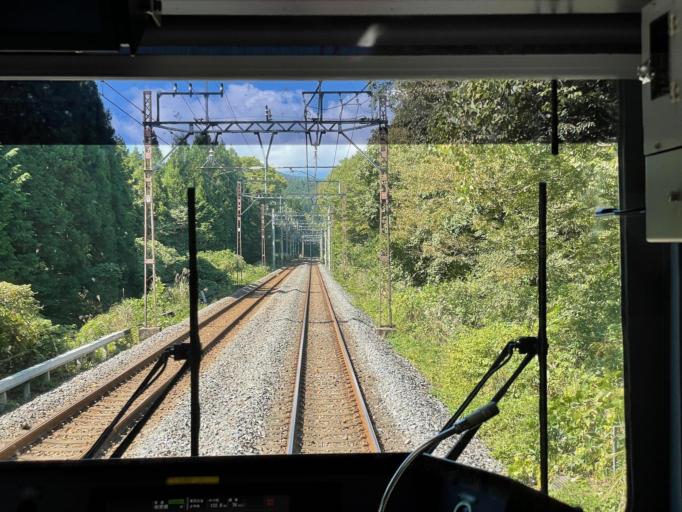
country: JP
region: Tochigi
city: Nikko
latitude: 36.7359
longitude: 139.6493
